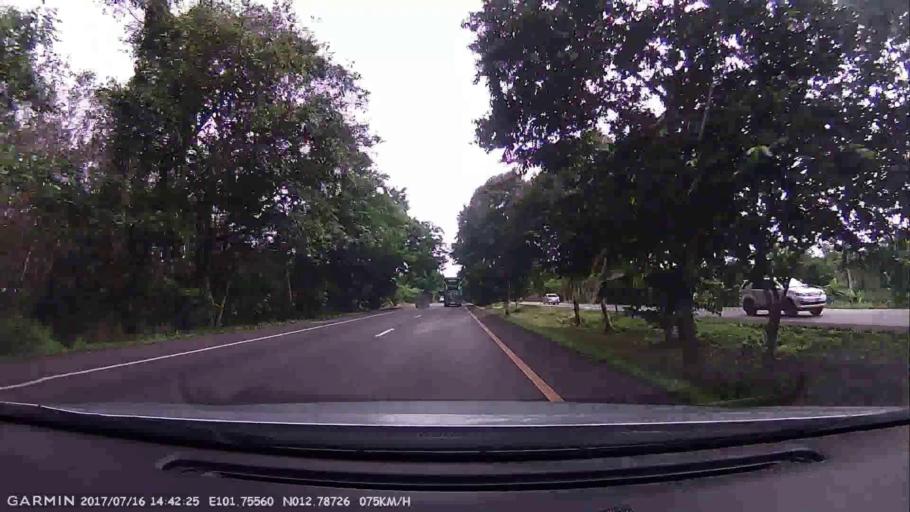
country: TH
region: Chanthaburi
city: Na Yai Am
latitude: 12.7872
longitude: 101.7553
